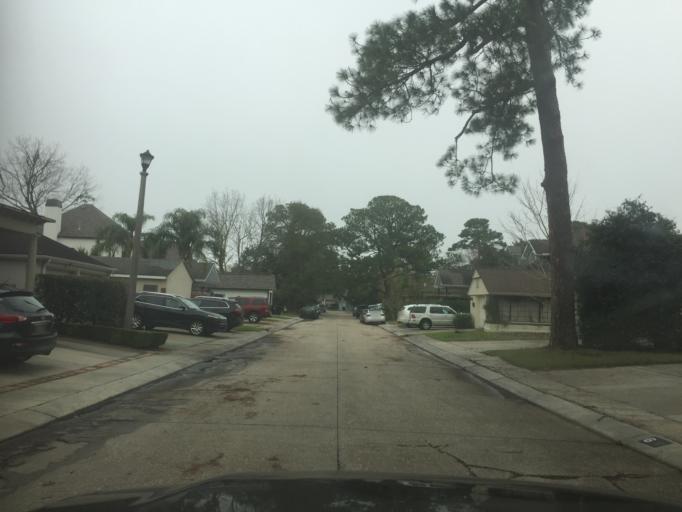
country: US
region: Louisiana
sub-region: Orleans Parish
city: New Orleans
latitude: 30.0190
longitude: -90.0932
